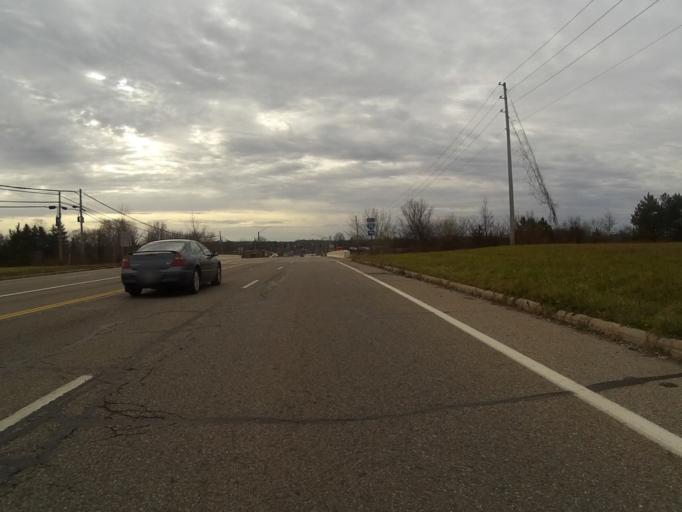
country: US
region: Ohio
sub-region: Portage County
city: Brimfield
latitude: 41.1082
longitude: -81.3476
